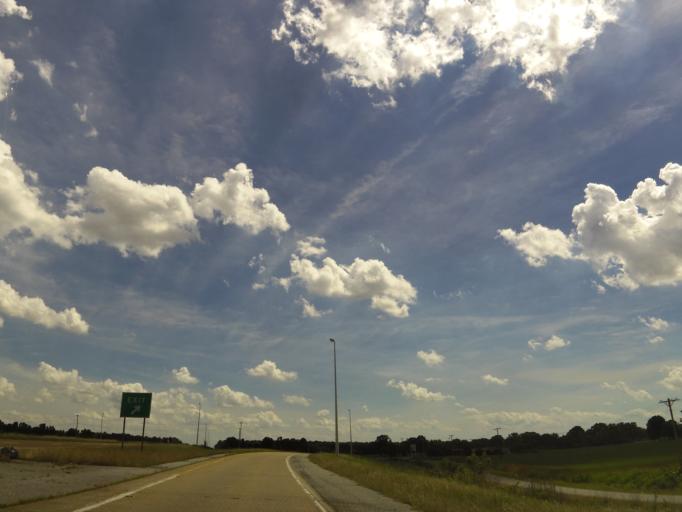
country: US
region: Tennessee
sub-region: Dyer County
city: Dyersburg
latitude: 36.0286
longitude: -89.3407
